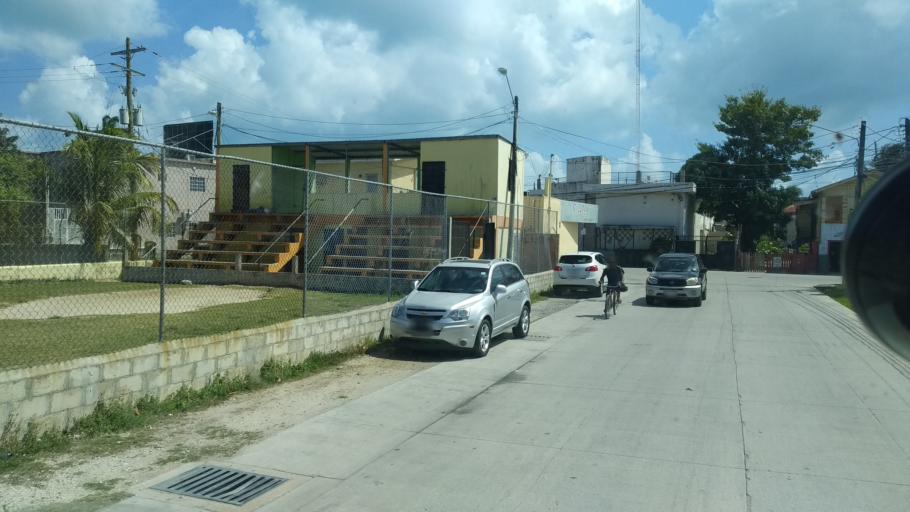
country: BZ
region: Belize
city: Belize City
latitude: 17.5027
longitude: -88.1904
